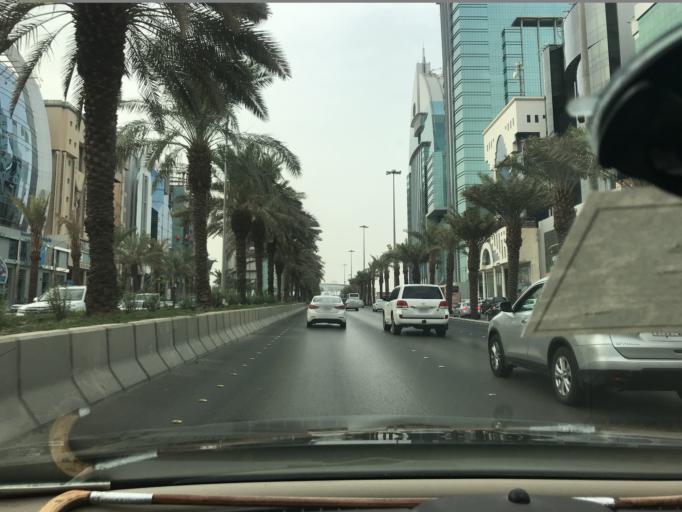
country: SA
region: Ar Riyad
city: Riyadh
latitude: 24.7046
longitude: 46.6759
